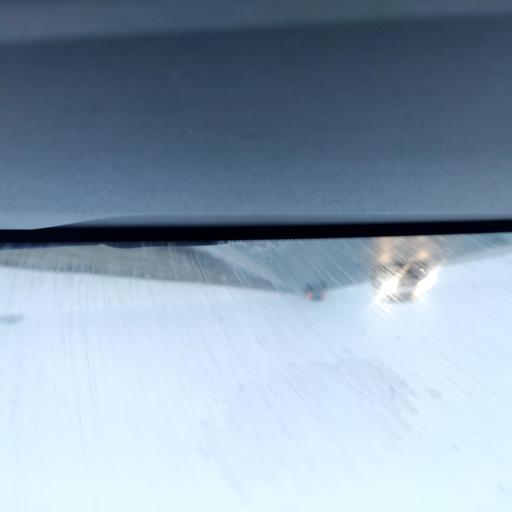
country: RU
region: Tatarstan
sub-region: Alekseyevskiy Rayon
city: Alekseyevskoye
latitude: 55.3113
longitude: 50.2163
